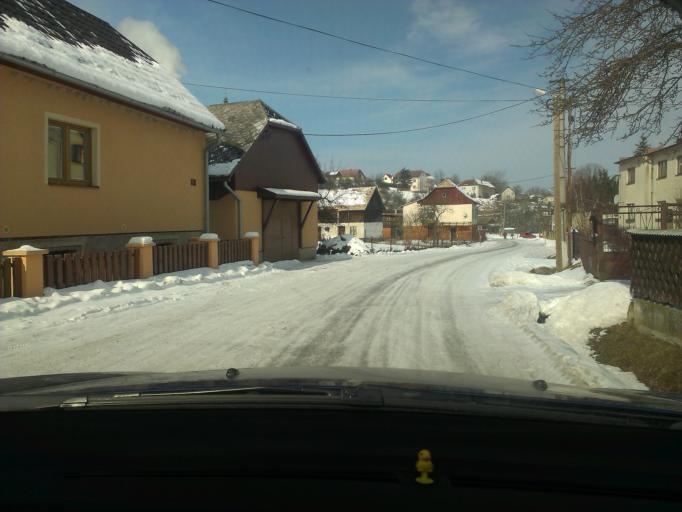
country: SK
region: Nitriansky
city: Handlova
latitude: 48.7849
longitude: 18.8391
